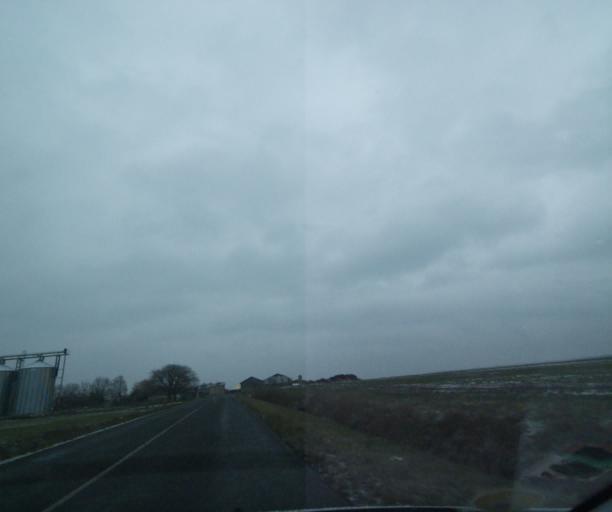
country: FR
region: Champagne-Ardenne
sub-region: Departement de la Haute-Marne
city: Wassy
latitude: 48.4313
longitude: 4.9971
